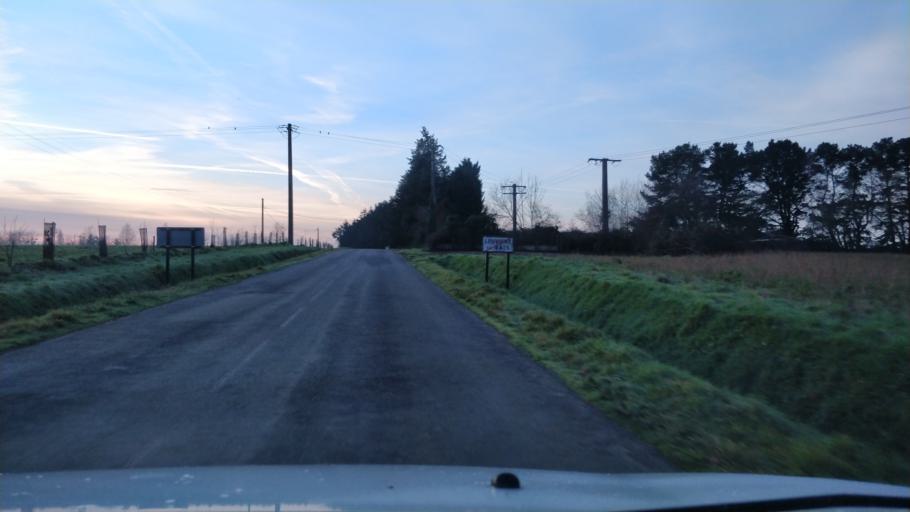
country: FR
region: Brittany
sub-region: Departement d'Ille-et-Vilaine
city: Louvigne-de-Bais
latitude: 48.0445
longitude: -1.3282
